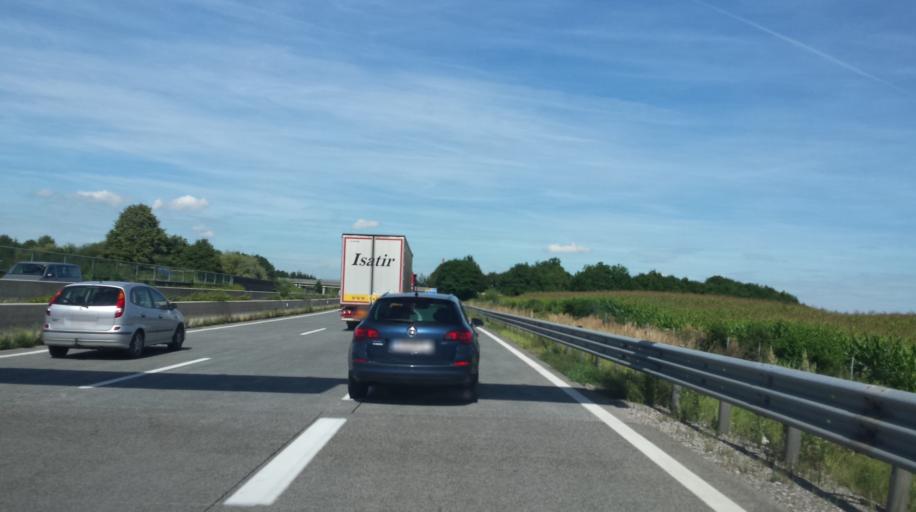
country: AT
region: Upper Austria
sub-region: Politischer Bezirk Vocklabruck
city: Attnang-Puchheim
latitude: 47.9540
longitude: 13.7290
